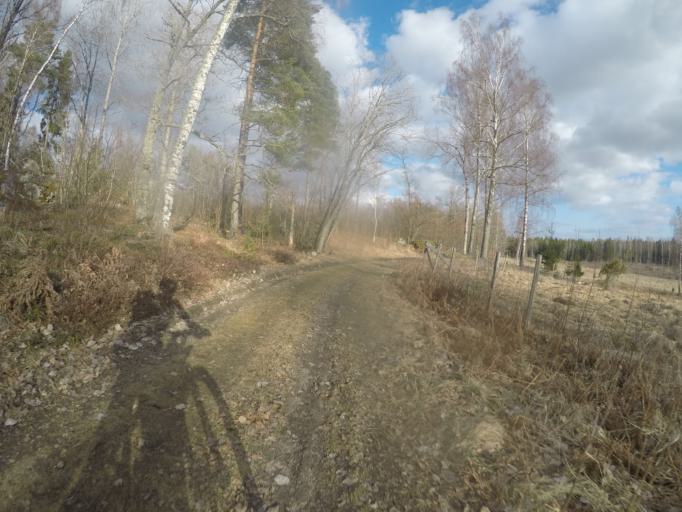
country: SE
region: Soedermanland
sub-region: Eskilstuna Kommun
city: Hallbybrunn
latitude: 59.3863
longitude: 16.3963
